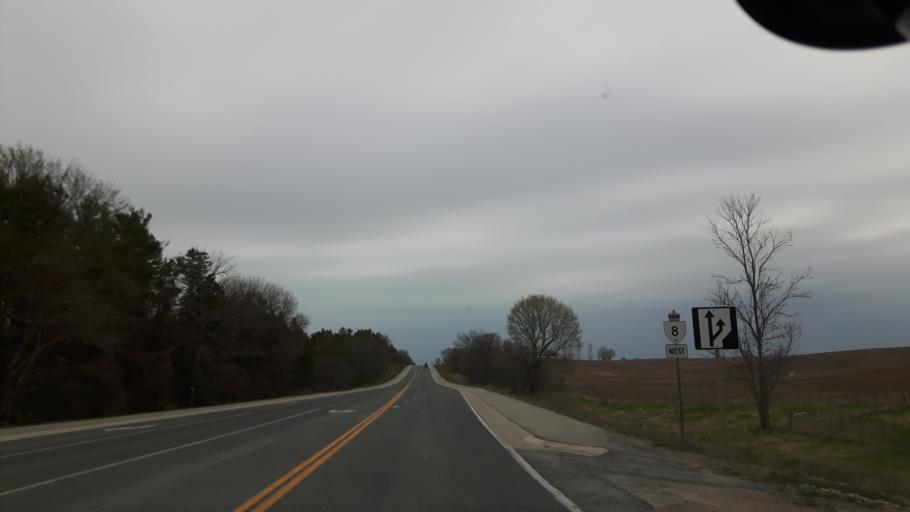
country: CA
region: Ontario
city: Goderich
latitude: 43.6471
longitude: -81.6023
